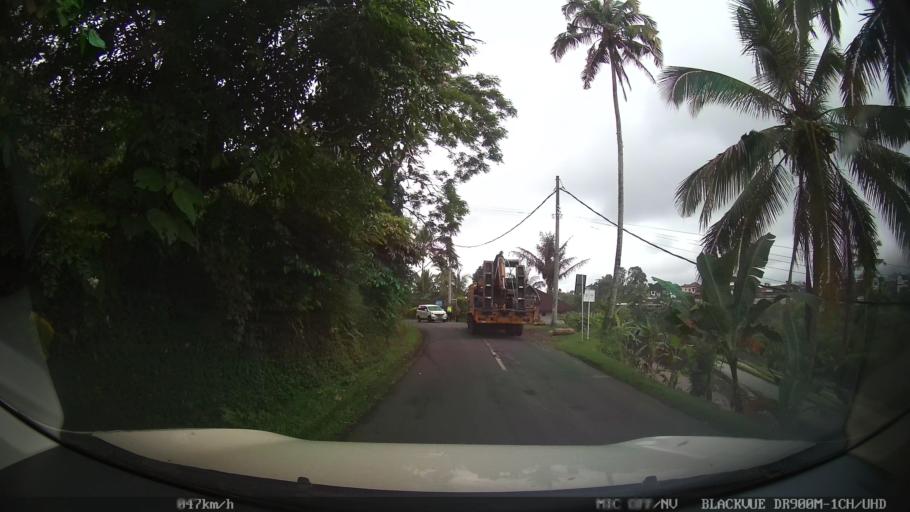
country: ID
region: Bali
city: Empalan
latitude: -8.3817
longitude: 115.1497
